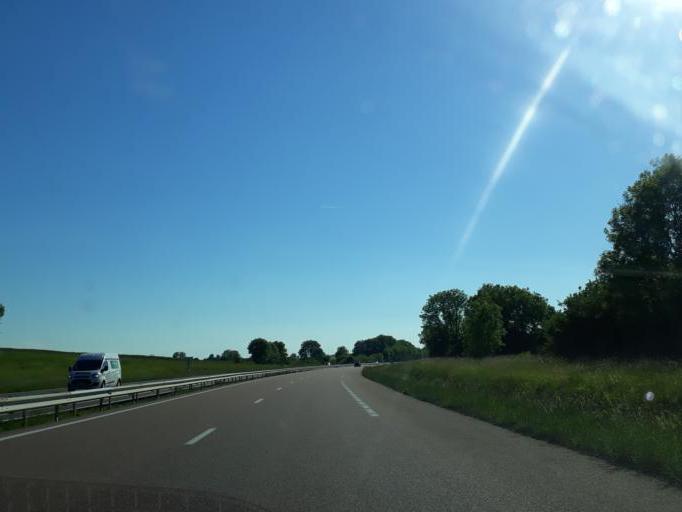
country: FR
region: Bourgogne
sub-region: Departement de la Cote-d'Or
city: Pouilly-en-Auxois
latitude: 47.2755
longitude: 4.6092
